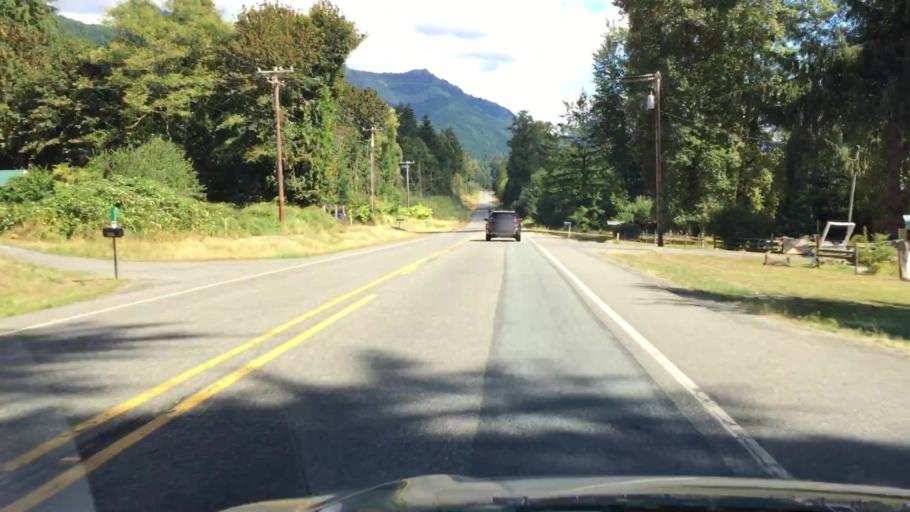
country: US
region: Washington
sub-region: Pierce County
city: Eatonville
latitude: 46.7569
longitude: -122.0035
